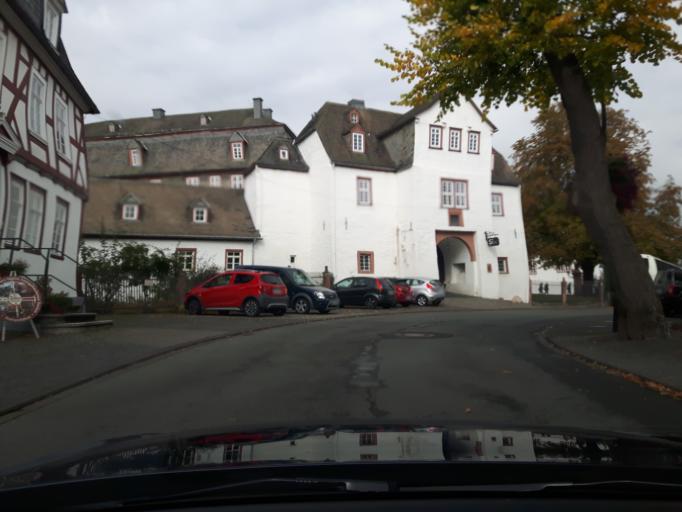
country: DE
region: North Rhine-Westphalia
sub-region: Regierungsbezirk Arnsberg
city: Bad Berleburg
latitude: 51.0507
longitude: 8.3890
